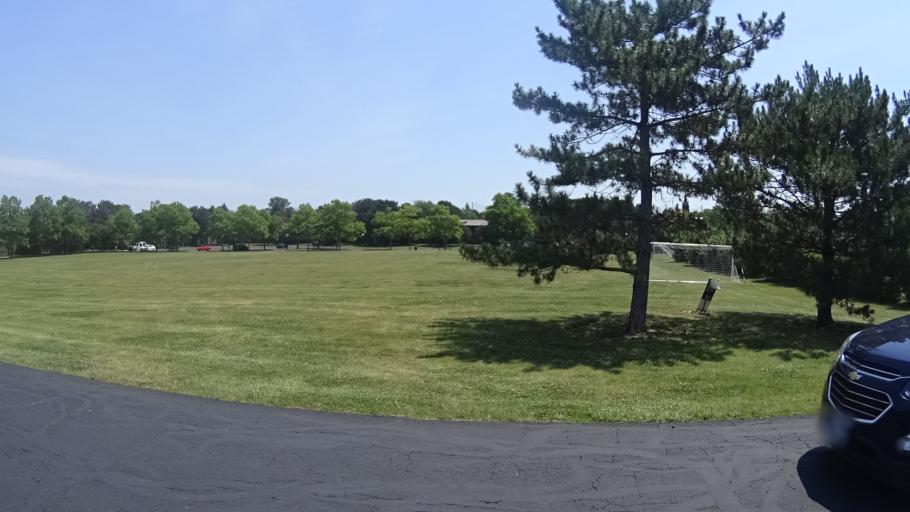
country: US
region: Ohio
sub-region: Erie County
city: Huron
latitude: 41.4097
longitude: -82.5980
